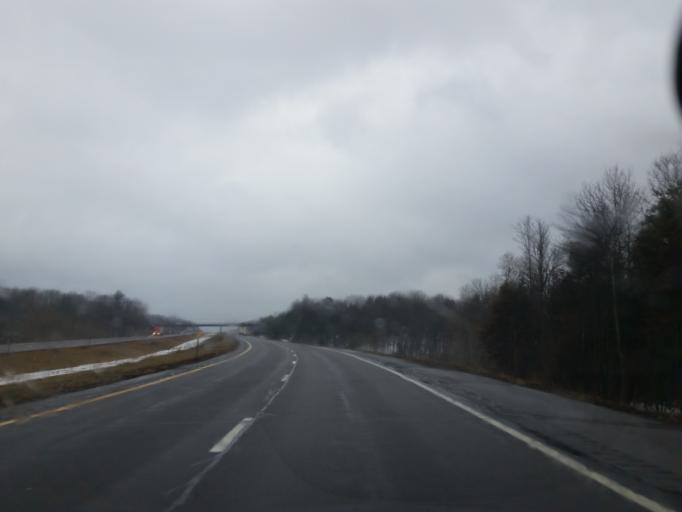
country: US
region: New York
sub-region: Chenango County
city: Lakeview
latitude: 42.3232
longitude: -75.9768
